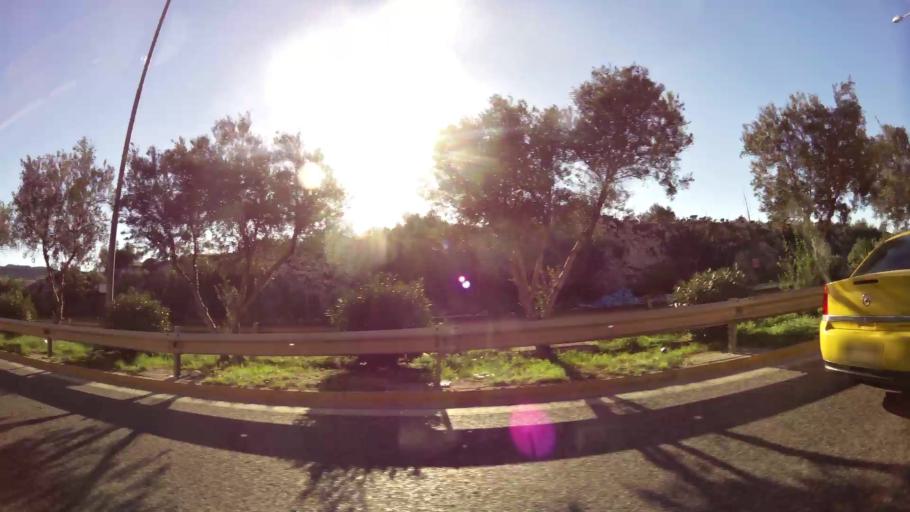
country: GR
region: Attica
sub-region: Nomarchia Athinas
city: Skaramangas
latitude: 37.9859
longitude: 23.5909
